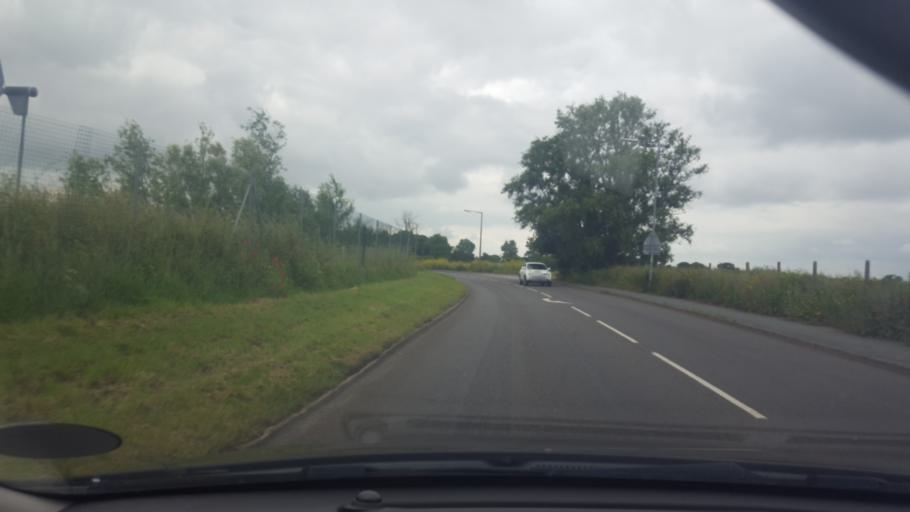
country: GB
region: England
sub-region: Essex
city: Saint Osyth
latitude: 51.7925
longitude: 1.1187
